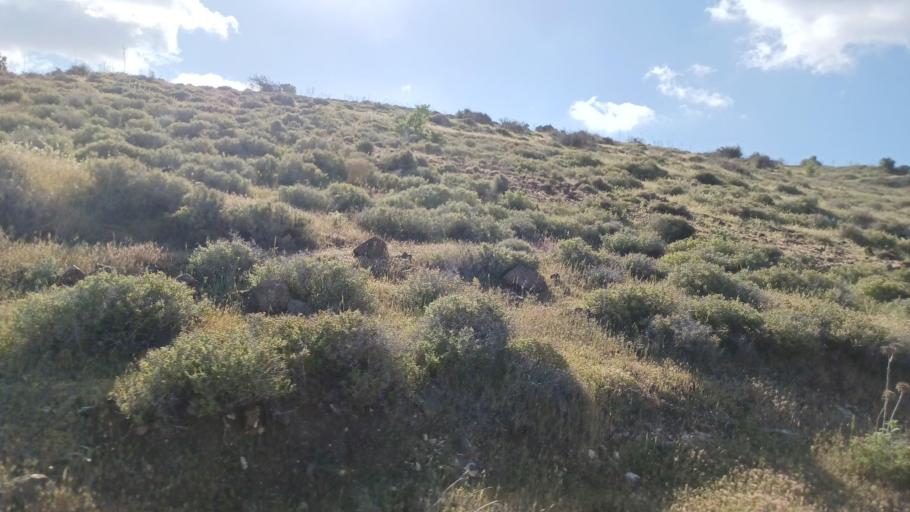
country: CY
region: Lefkosia
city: Peristerona
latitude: 35.0662
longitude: 33.0527
